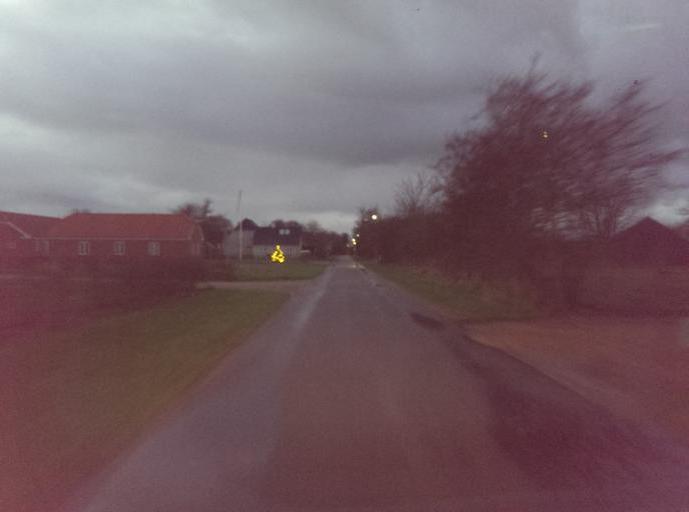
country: DK
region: South Denmark
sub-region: Esbjerg Kommune
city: Bramming
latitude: 55.4446
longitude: 8.6527
